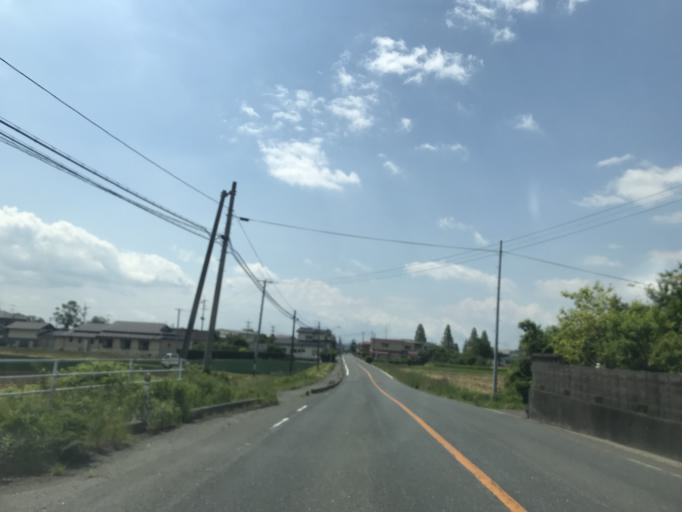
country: JP
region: Miyagi
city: Kogota
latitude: 38.6081
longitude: 141.0221
